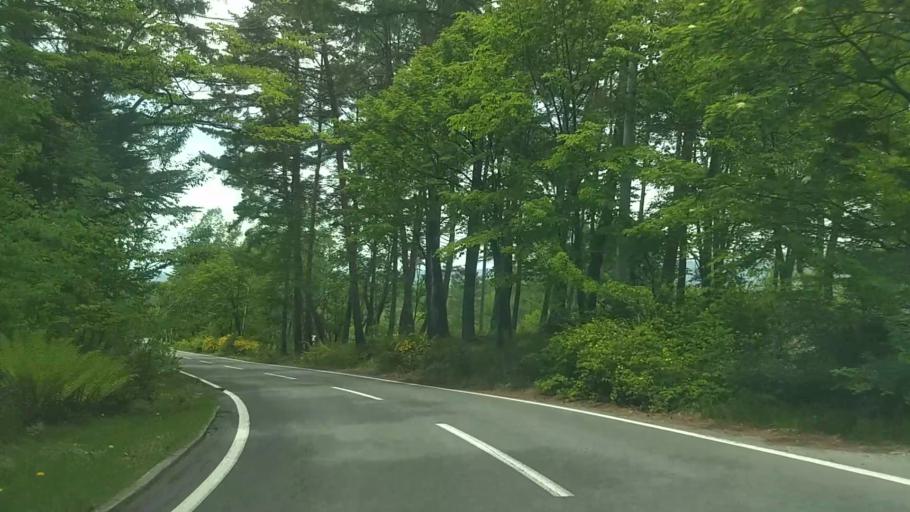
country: JP
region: Nagano
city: Chino
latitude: 36.0352
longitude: 138.2640
